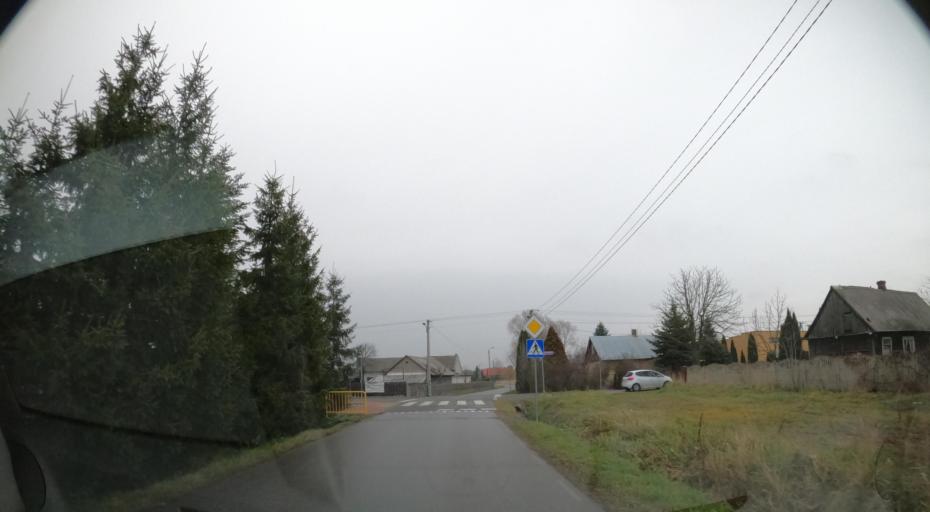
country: PL
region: Masovian Voivodeship
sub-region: Radom
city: Radom
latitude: 51.4158
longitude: 21.2227
